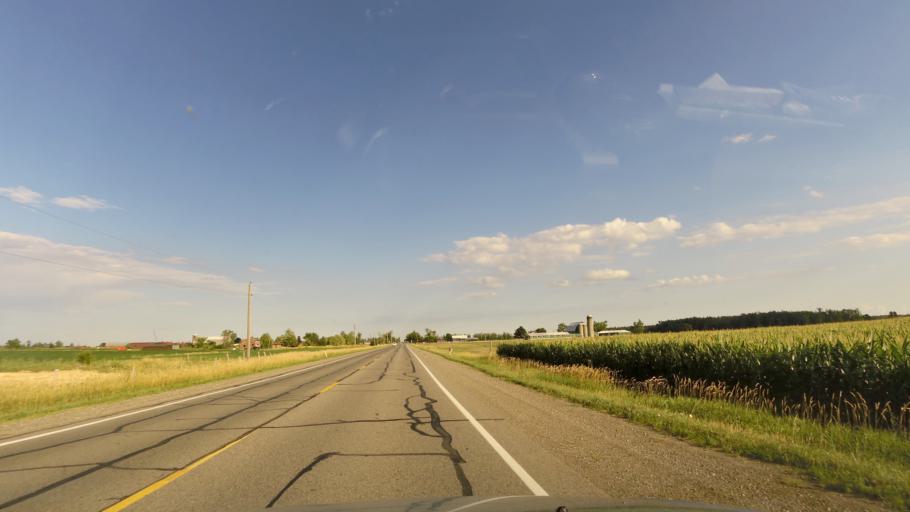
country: CA
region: Ontario
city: Brampton
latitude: 43.7069
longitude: -79.8840
